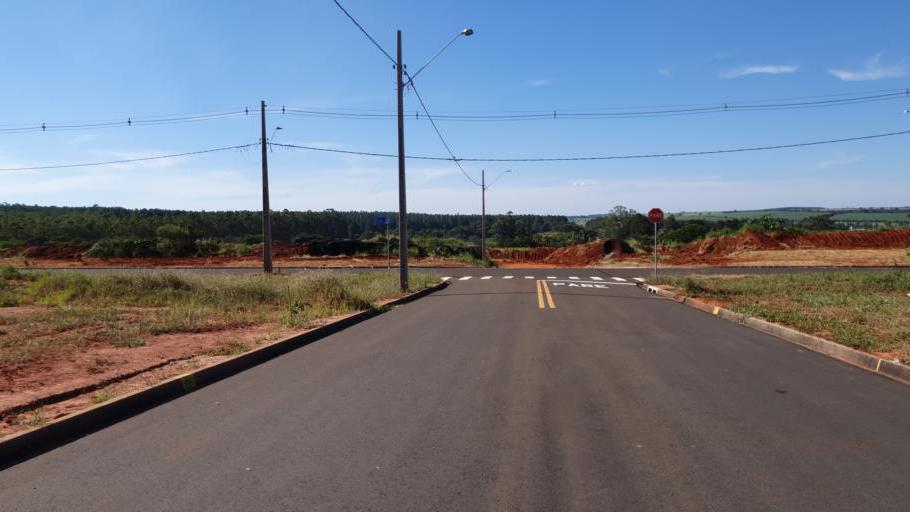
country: BR
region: Sao Paulo
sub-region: Paraguacu Paulista
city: Paraguacu Paulista
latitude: -22.3994
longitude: -50.5763
